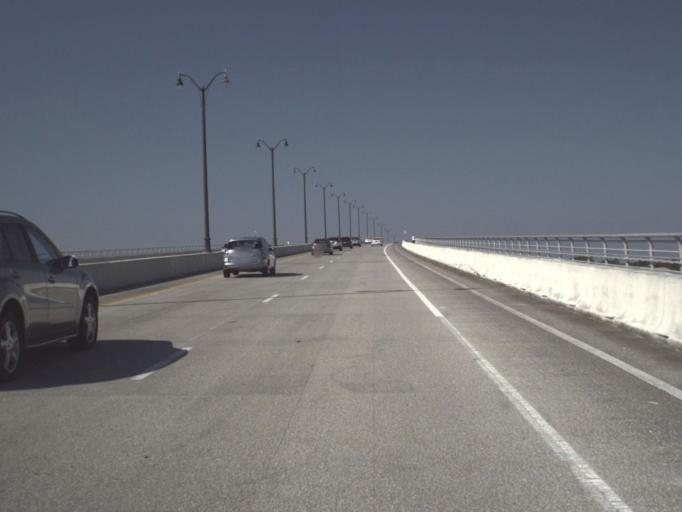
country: US
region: Florida
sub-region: Martin County
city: Sewall's Point
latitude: 27.2008
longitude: -80.2048
